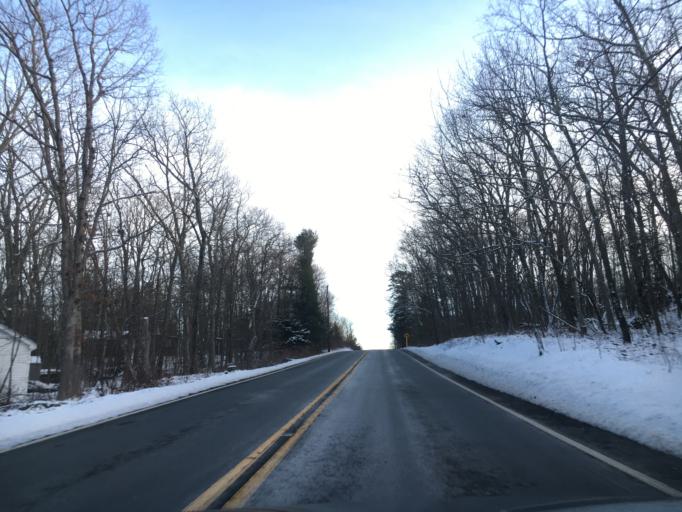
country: US
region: Pennsylvania
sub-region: Pike County
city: Hemlock Farms
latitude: 41.2829
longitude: -75.0919
